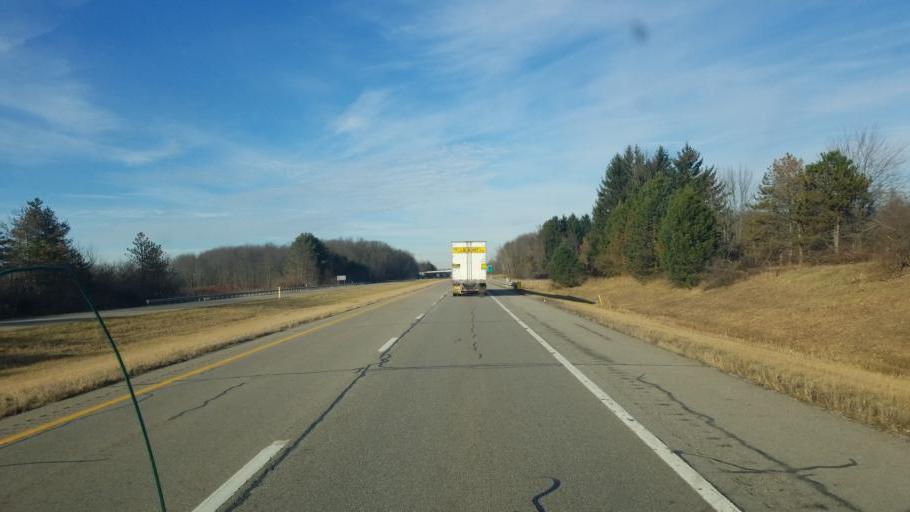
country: US
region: Ohio
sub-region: Ashtabula County
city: Orwell
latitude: 41.5147
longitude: -80.7132
